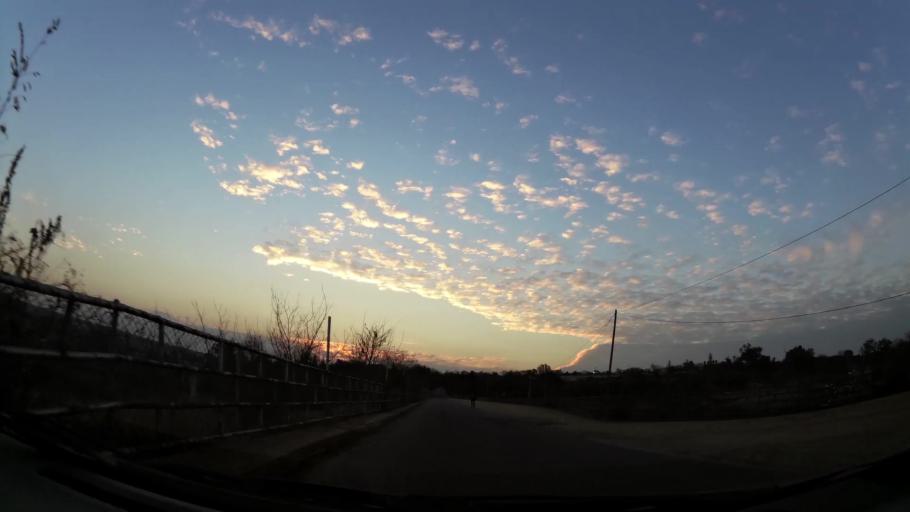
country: ZA
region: Gauteng
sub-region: City of Johannesburg Metropolitan Municipality
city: Midrand
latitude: -26.0100
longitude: 28.0499
